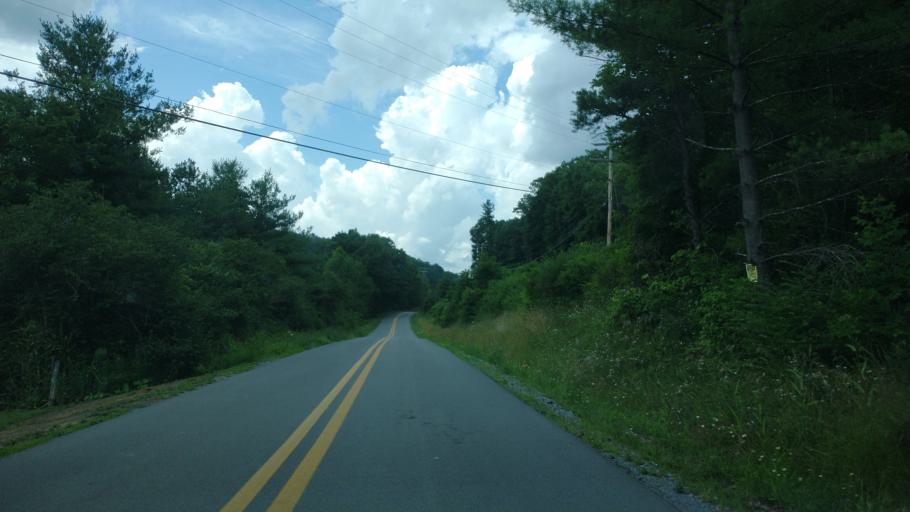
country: US
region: West Virginia
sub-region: Mercer County
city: Athens
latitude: 37.4418
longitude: -81.0637
